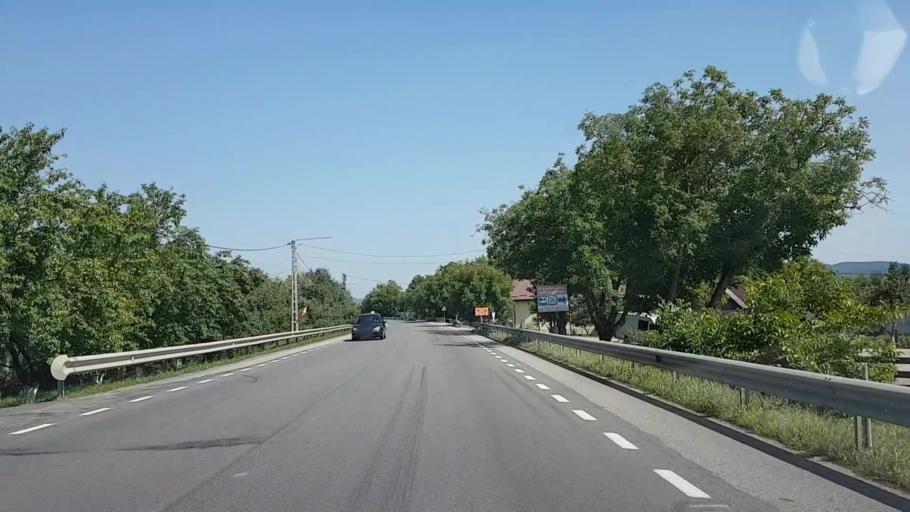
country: RO
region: Bistrita-Nasaud
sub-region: Comuna Uriu
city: Cristestii Ciceului
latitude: 47.1958
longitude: 24.0813
